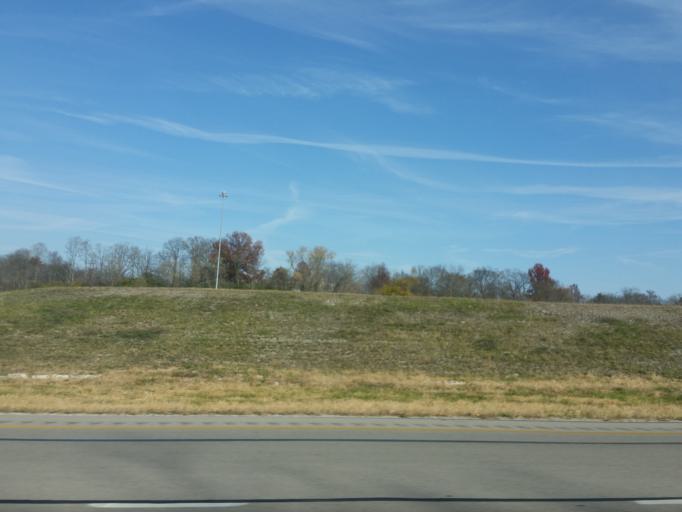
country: US
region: Kentucky
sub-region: Campbell County
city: Highland Heights
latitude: 39.0428
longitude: -84.4574
